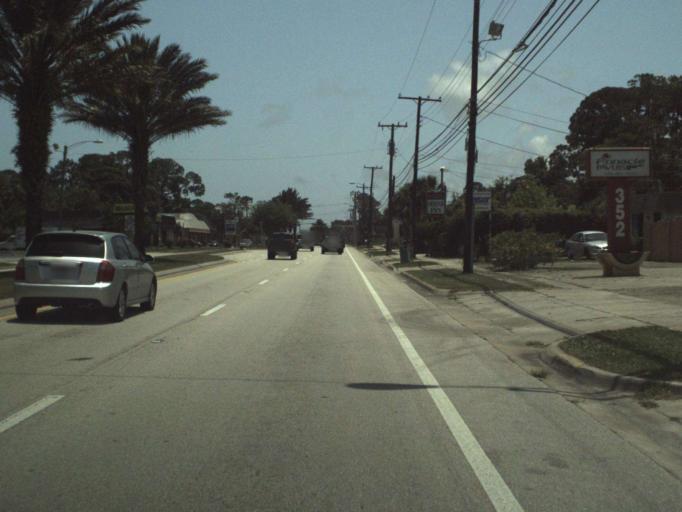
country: US
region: Florida
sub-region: Volusia County
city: Ormond Beach
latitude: 29.2743
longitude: -81.0577
